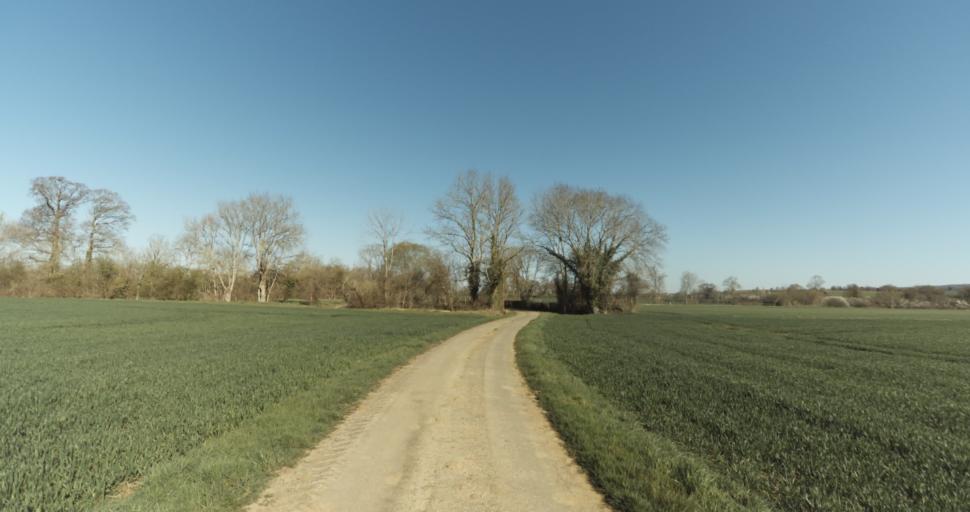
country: FR
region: Lower Normandy
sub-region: Departement du Calvados
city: Saint-Pierre-sur-Dives
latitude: 48.9513
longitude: 0.0230
